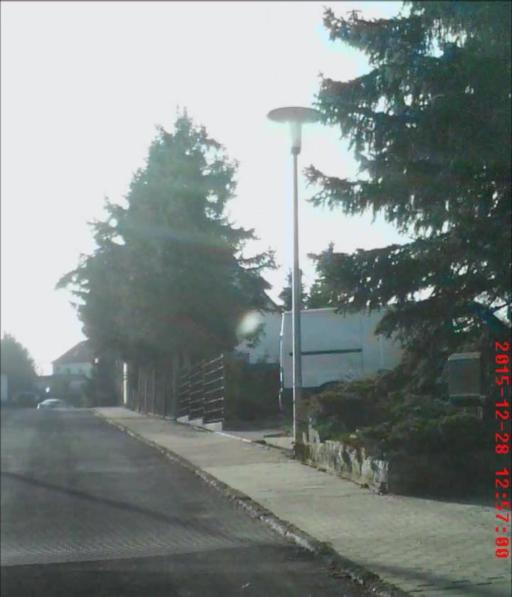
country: DE
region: Thuringia
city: Niederrossla
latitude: 51.0222
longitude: 11.4775
